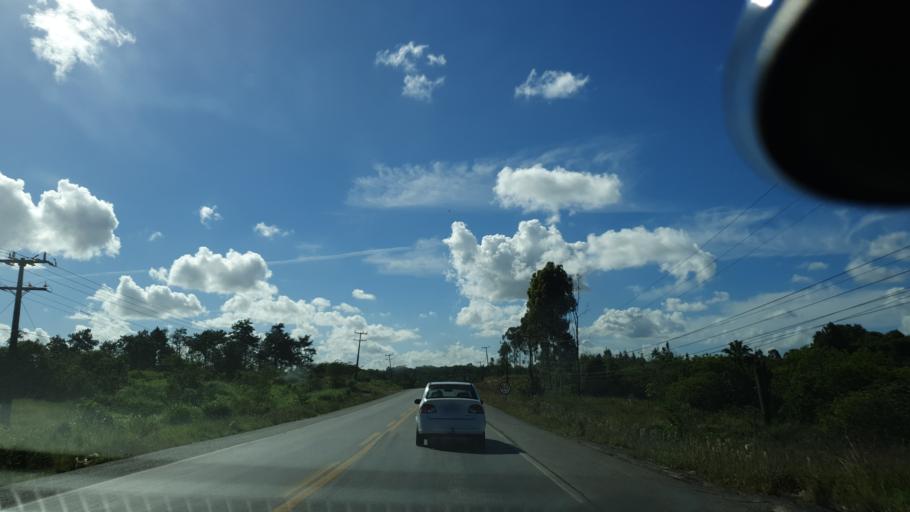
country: BR
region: Bahia
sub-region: Camacari
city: Camacari
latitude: -12.6843
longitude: -38.2769
